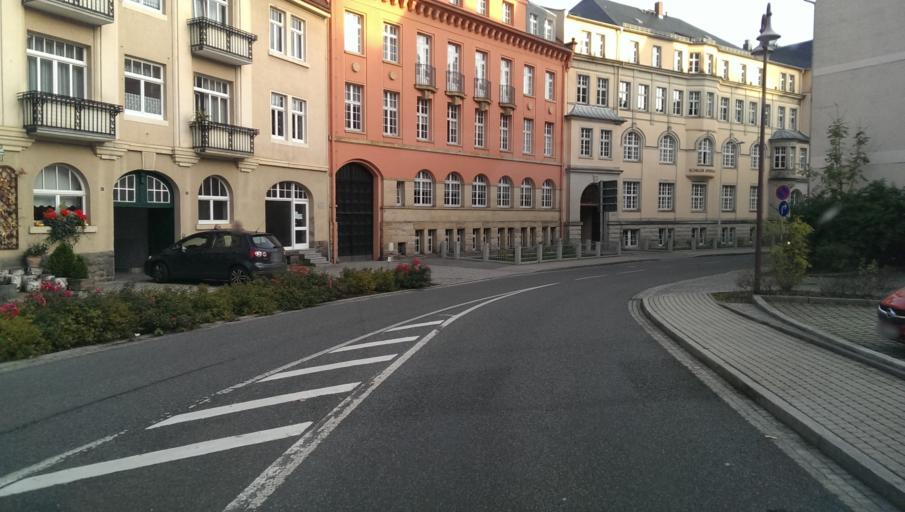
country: DE
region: Saxony
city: Sebnitz
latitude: 50.9695
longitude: 14.2707
